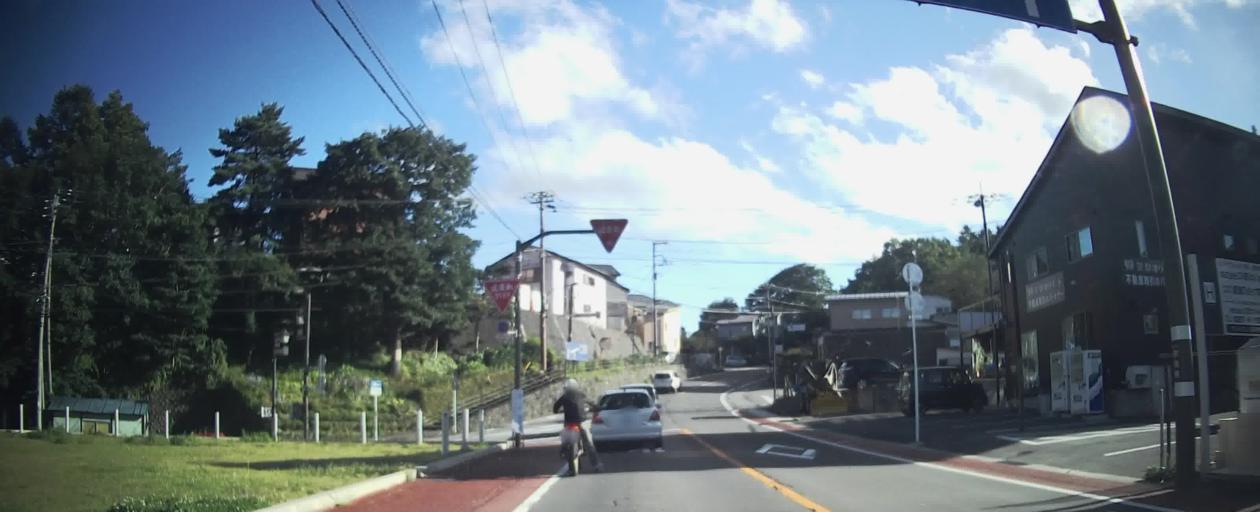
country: JP
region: Gunma
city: Nakanojomachi
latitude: 36.6189
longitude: 138.5934
